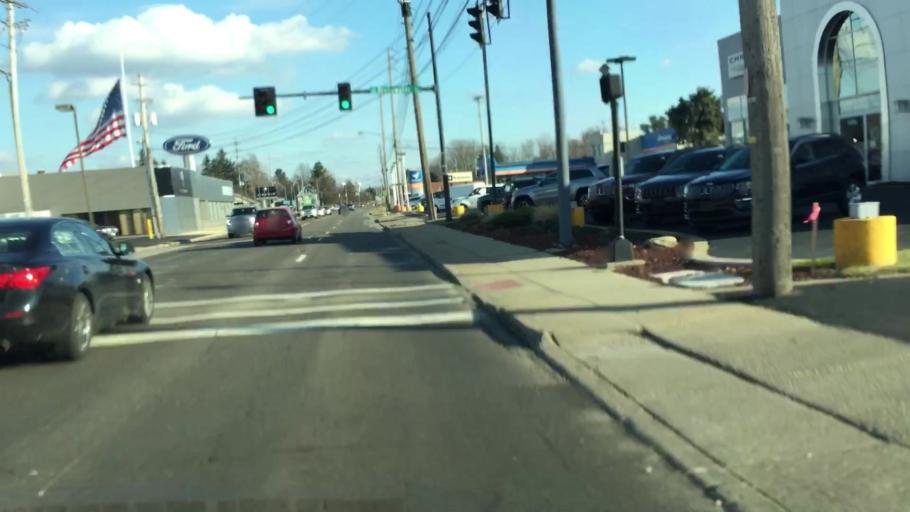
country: US
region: Ohio
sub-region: Portage County
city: Kent
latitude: 41.1515
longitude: -81.3816
